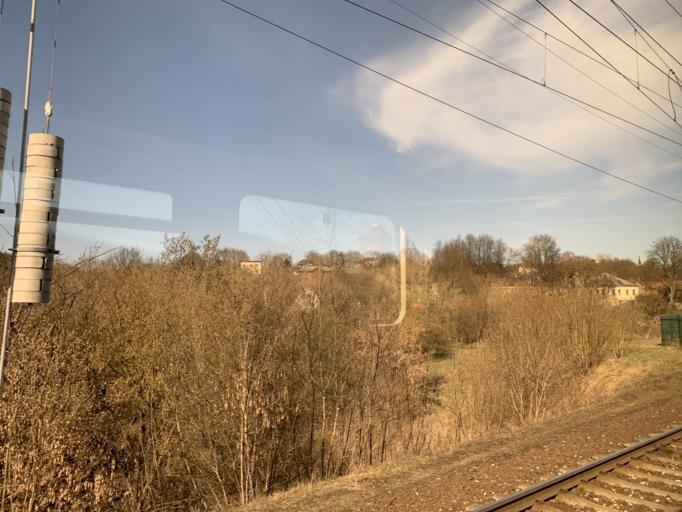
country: LT
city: Skaidiskes
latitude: 54.6931
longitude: 25.3985
